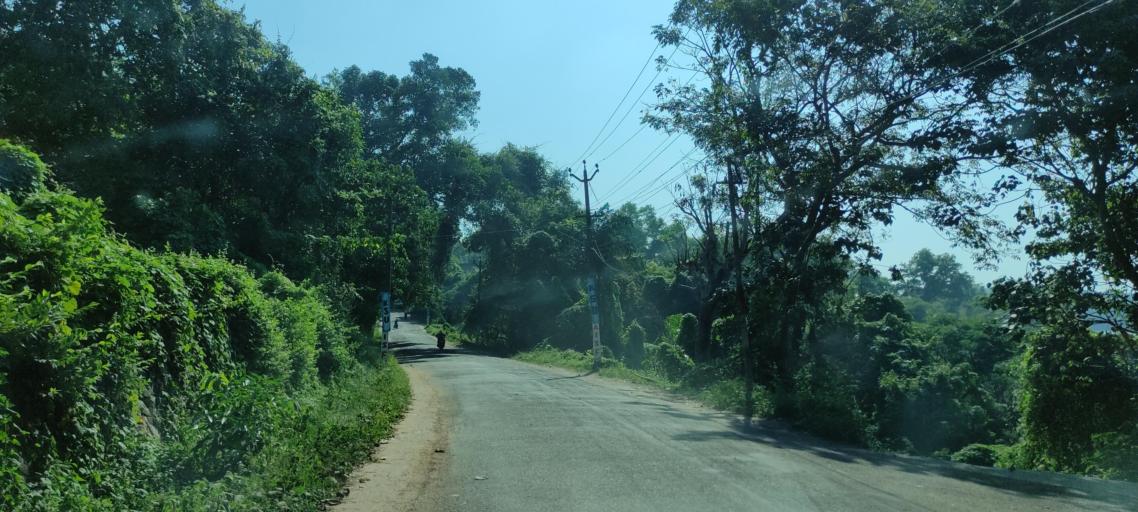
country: IN
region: Kerala
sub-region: Kollam
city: Panmana
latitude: 9.0416
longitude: 76.6284
